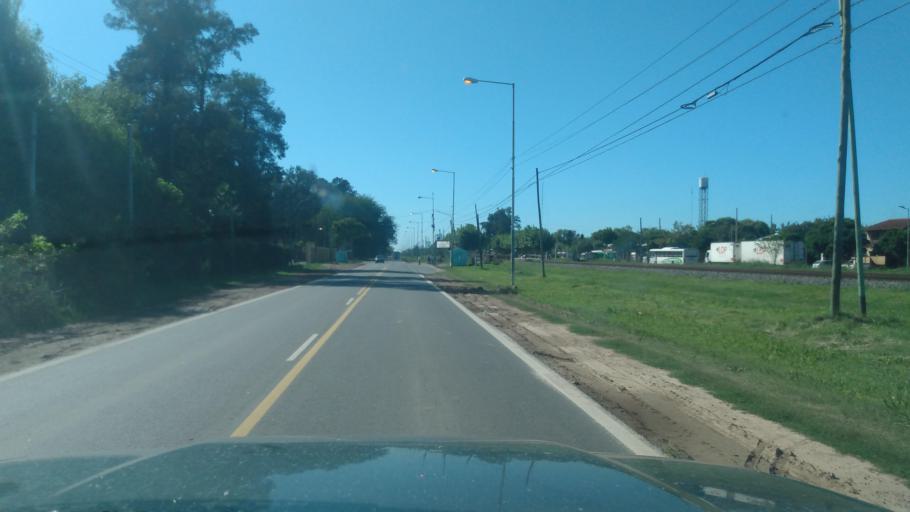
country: AR
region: Buenos Aires
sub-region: Partido de General Rodriguez
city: General Rodriguez
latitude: -34.5978
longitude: -58.9996
